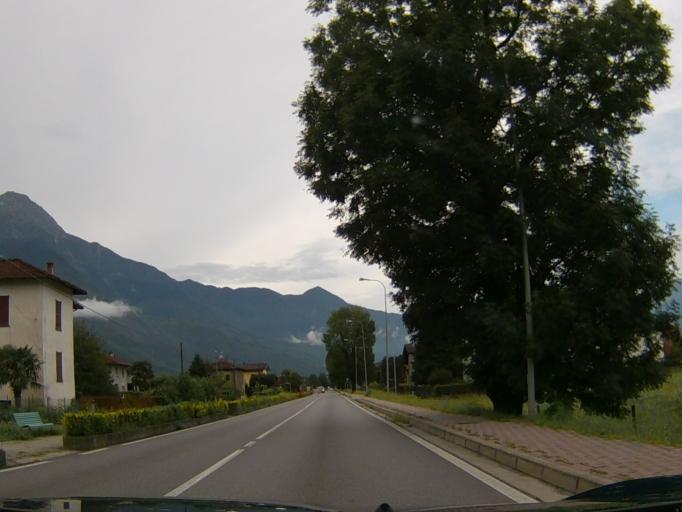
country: IT
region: Lombardy
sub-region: Provincia di Sondrio
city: Dubino
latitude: 46.1656
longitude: 9.4271
